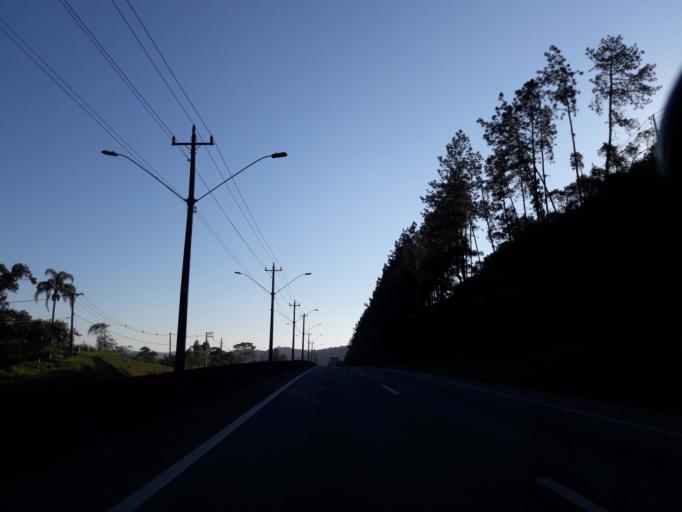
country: BR
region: Sao Paulo
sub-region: Sao Lourenco Da Serra
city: Sao Lourenco da Serra
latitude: -23.8707
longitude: -46.9598
